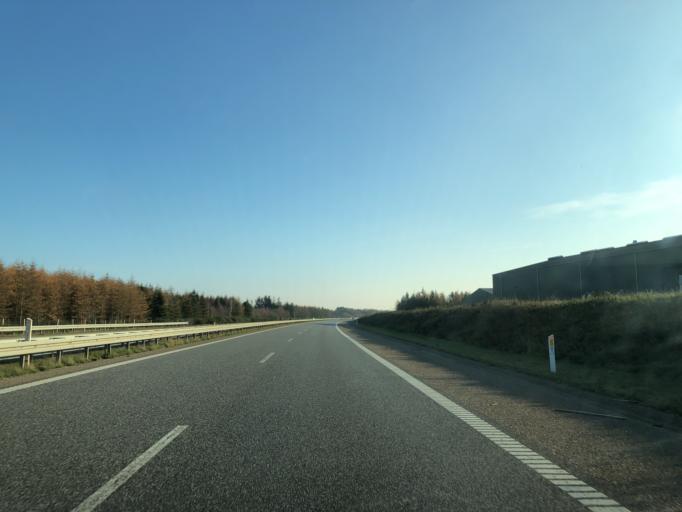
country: DK
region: Central Jutland
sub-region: Ikast-Brande Kommune
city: Brande
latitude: 55.9080
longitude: 9.1985
